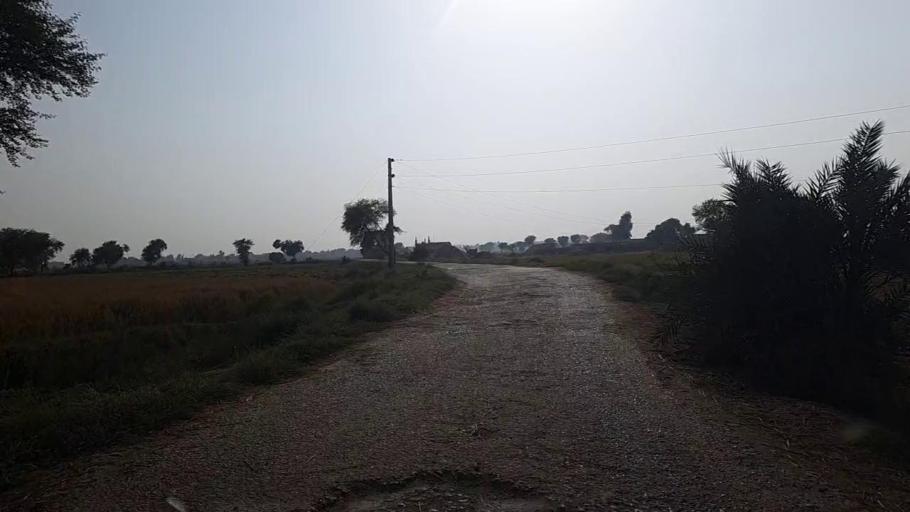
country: PK
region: Sindh
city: Kandhkot
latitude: 28.2853
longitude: 69.2581
